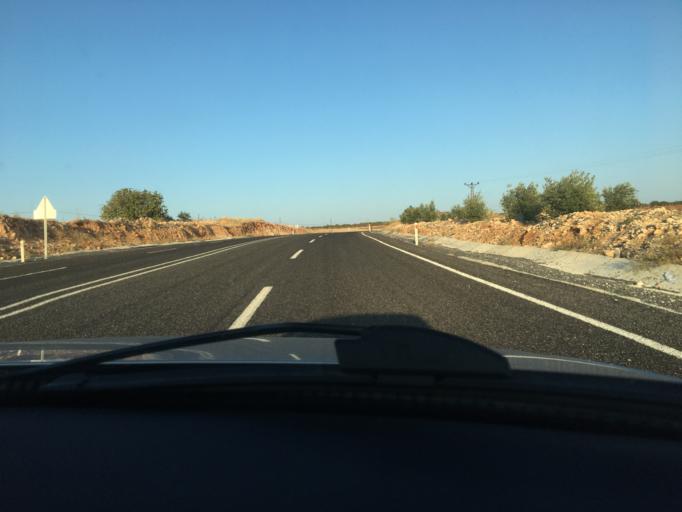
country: TR
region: Sanliurfa
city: Halfeti
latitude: 37.2421
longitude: 37.8851
